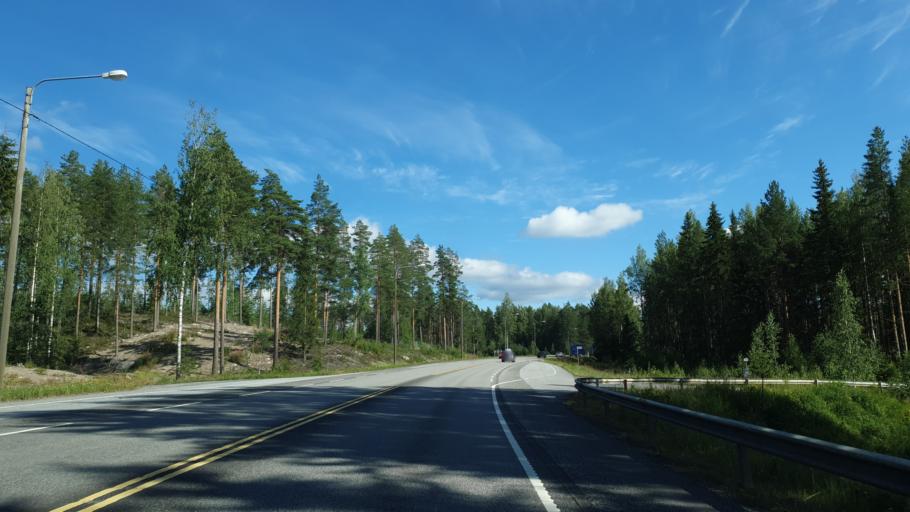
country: FI
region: Central Finland
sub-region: Jyvaeskylae
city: Toivakka
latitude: 62.2507
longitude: 26.1226
